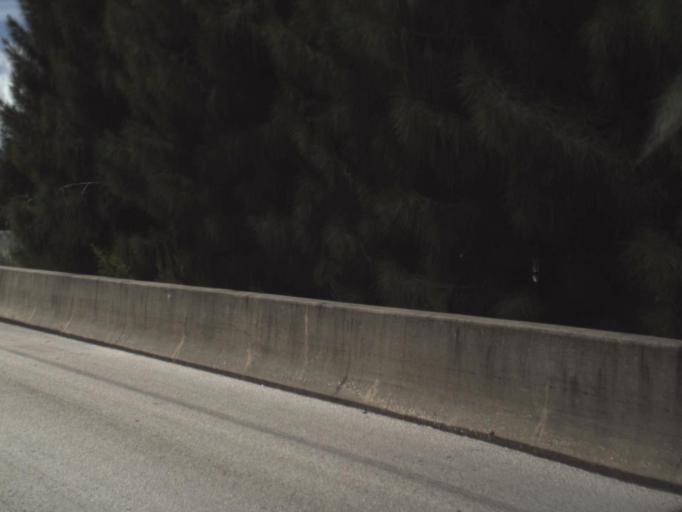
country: US
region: Florida
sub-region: Pinellas County
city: South Highpoint
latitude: 27.9201
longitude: -82.6989
